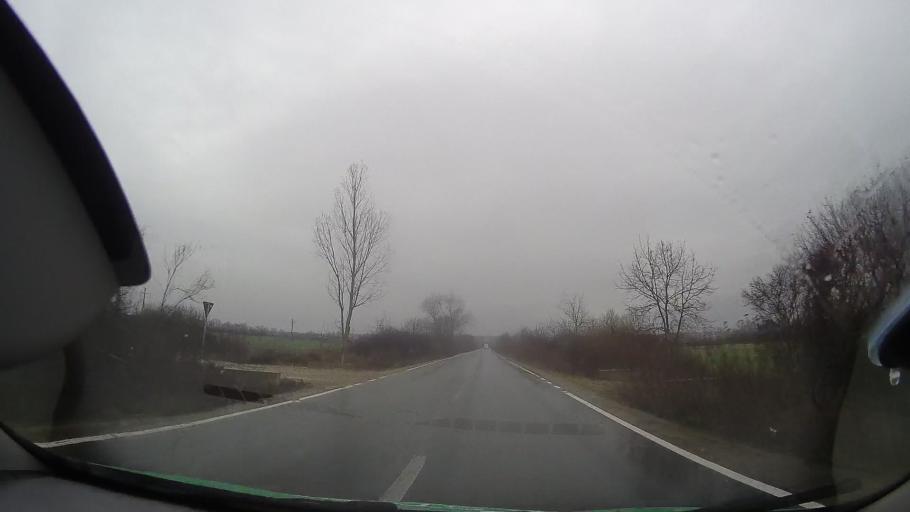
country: RO
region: Bihor
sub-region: Comuna Tinca
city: Tinca
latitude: 46.7584
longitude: 21.9355
